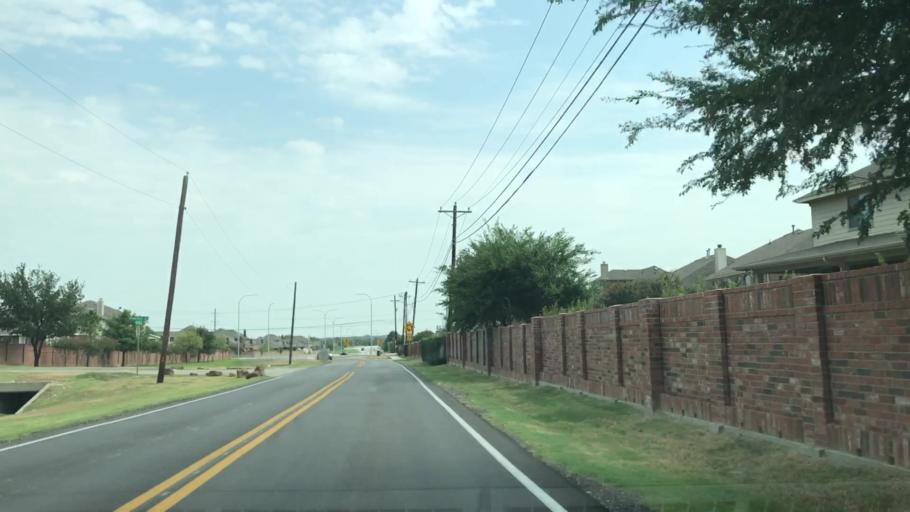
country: US
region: Texas
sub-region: Tarrant County
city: Keller
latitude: 32.9224
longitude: -97.2724
